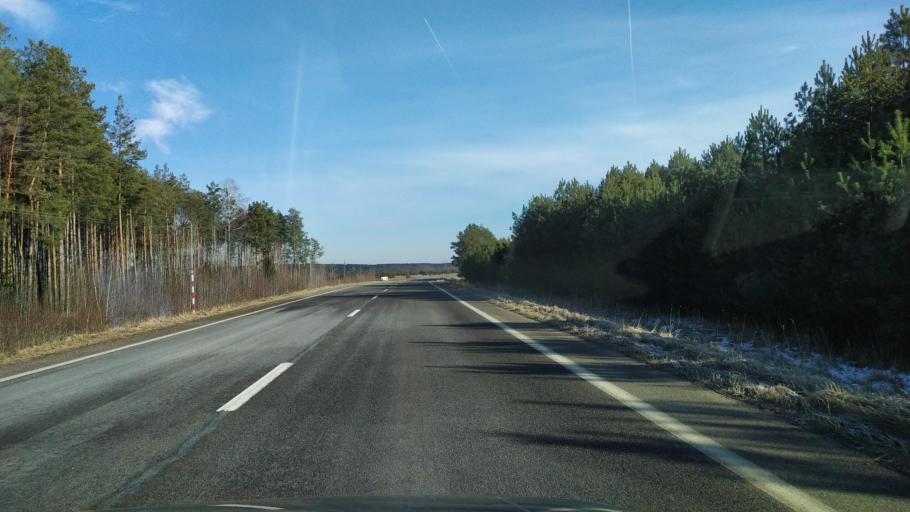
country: BY
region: Brest
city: Kamyanyets
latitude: 52.3984
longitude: 23.9911
